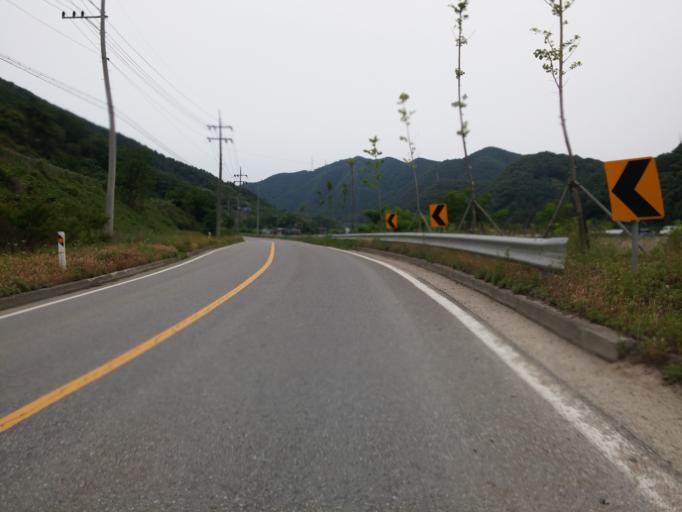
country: KR
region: Chungcheongbuk-do
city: Okcheon
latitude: 36.2595
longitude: 127.5173
